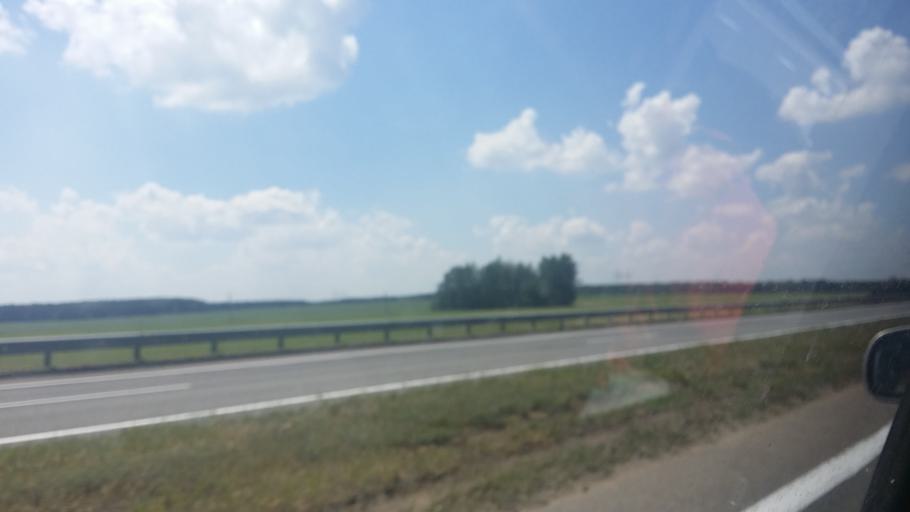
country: BY
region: Minsk
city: Smilavichy
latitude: 53.7641
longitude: 28.1258
